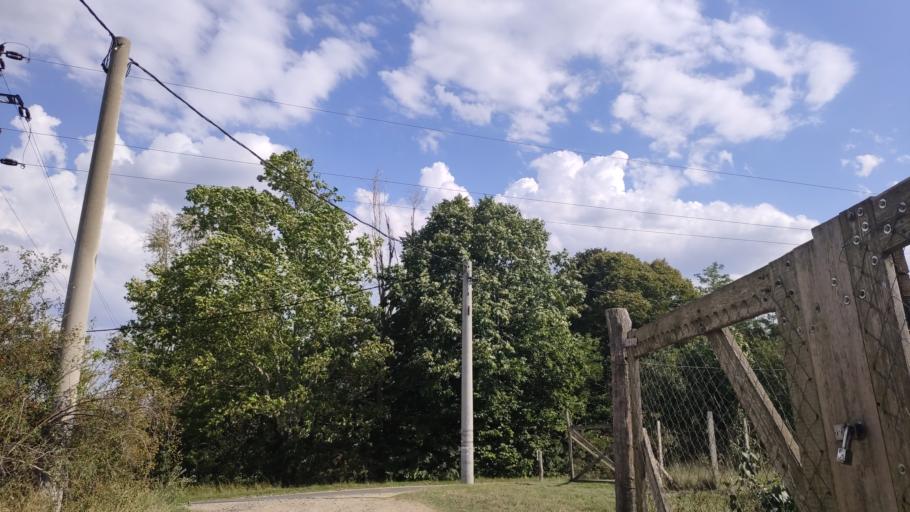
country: HU
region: Pest
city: Toeroekbalint
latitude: 47.4589
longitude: 18.8715
